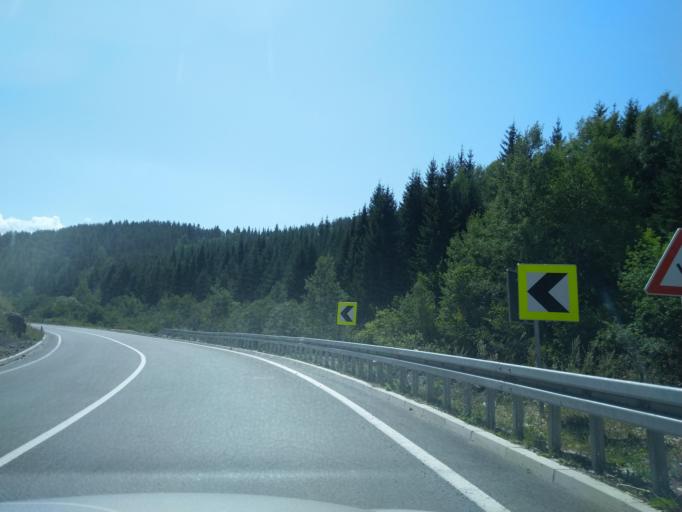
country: RS
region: Central Serbia
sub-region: Zlatiborski Okrug
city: Sjenica
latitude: 43.2815
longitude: 19.9567
